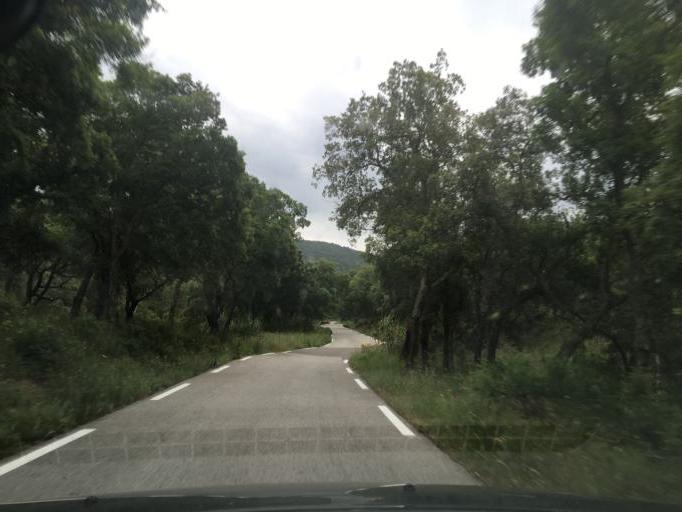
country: FR
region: Provence-Alpes-Cote d'Azur
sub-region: Departement du Var
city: Pignans
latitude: 43.2286
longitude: 6.2171
